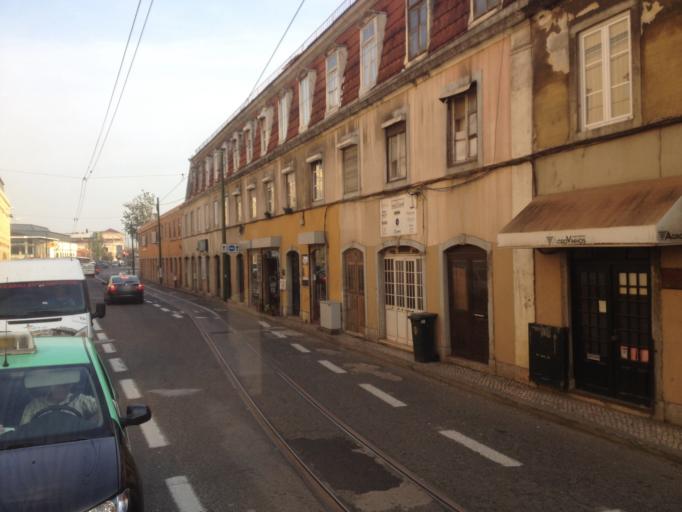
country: PT
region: Setubal
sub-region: Almada
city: Pragal
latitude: 38.7045
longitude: -9.1760
